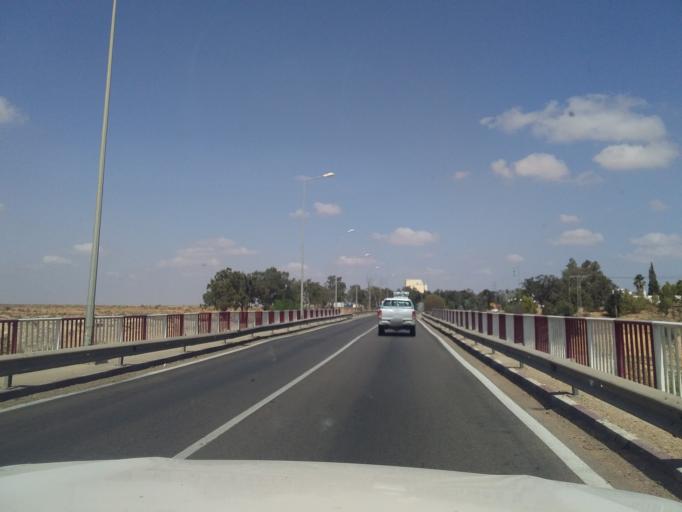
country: TN
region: Madanin
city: Medenine
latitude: 33.5943
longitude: 10.3123
